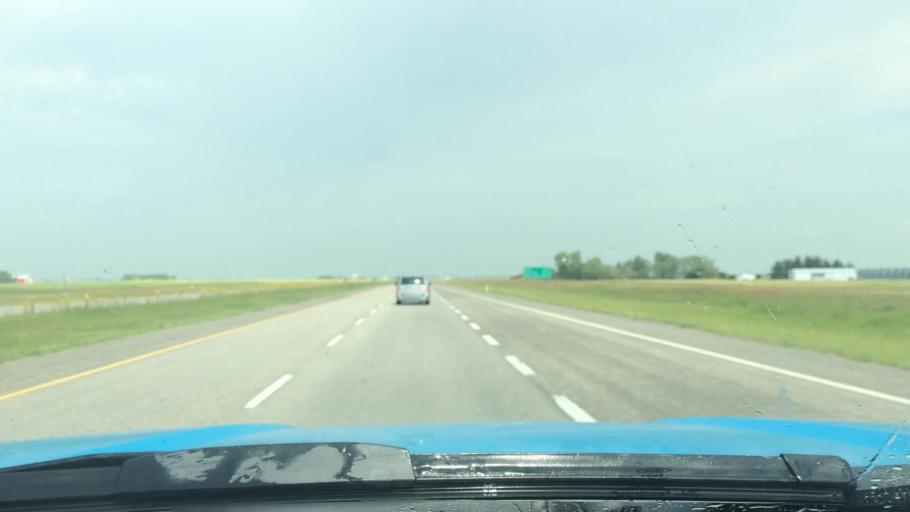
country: CA
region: Alberta
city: Didsbury
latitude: 51.6703
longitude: -114.0253
